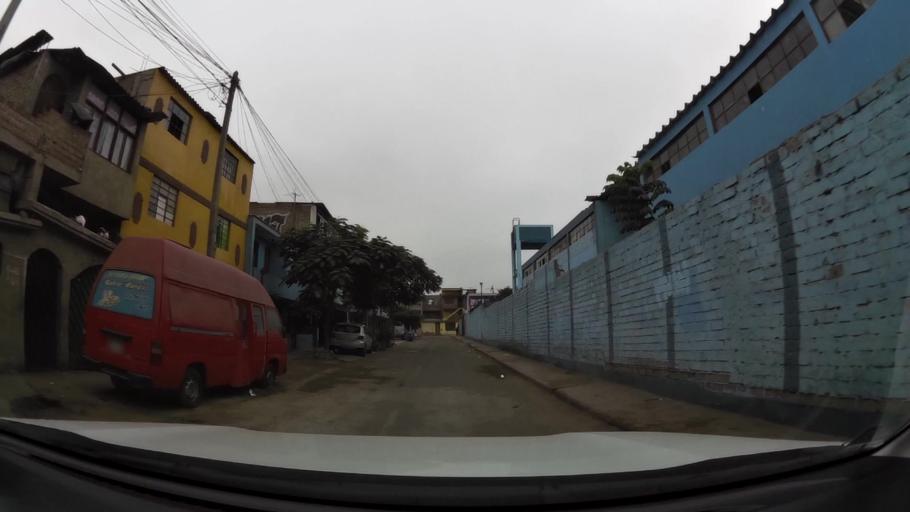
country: PE
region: Lima
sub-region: Lima
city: Surco
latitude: -12.1505
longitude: -76.9779
